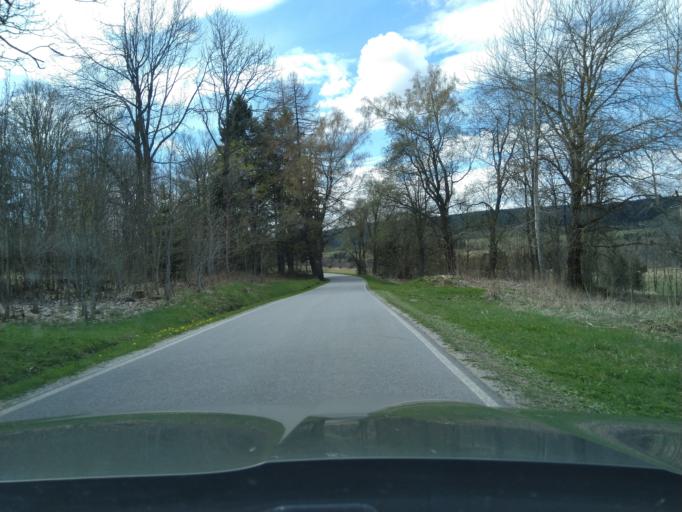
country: CZ
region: Jihocesky
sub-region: Okres Prachatice
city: Zdikov
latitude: 49.0425
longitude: 13.6692
